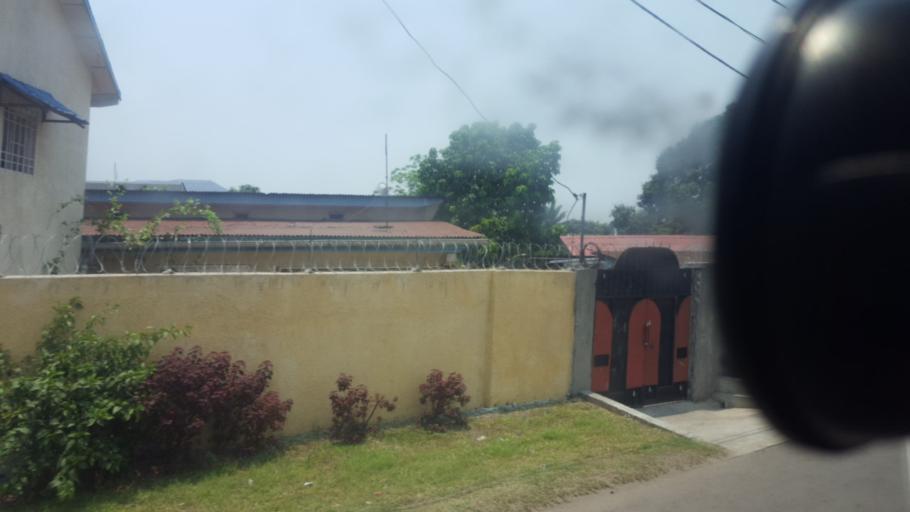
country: CD
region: Kinshasa
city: Masina
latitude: -4.3852
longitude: 15.3559
